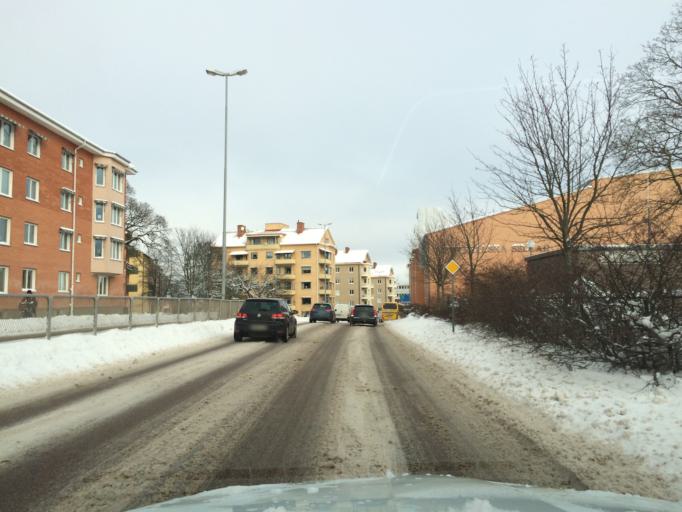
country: SE
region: Vaestmanland
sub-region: Vasteras
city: Vasteras
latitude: 59.6072
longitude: 16.5350
